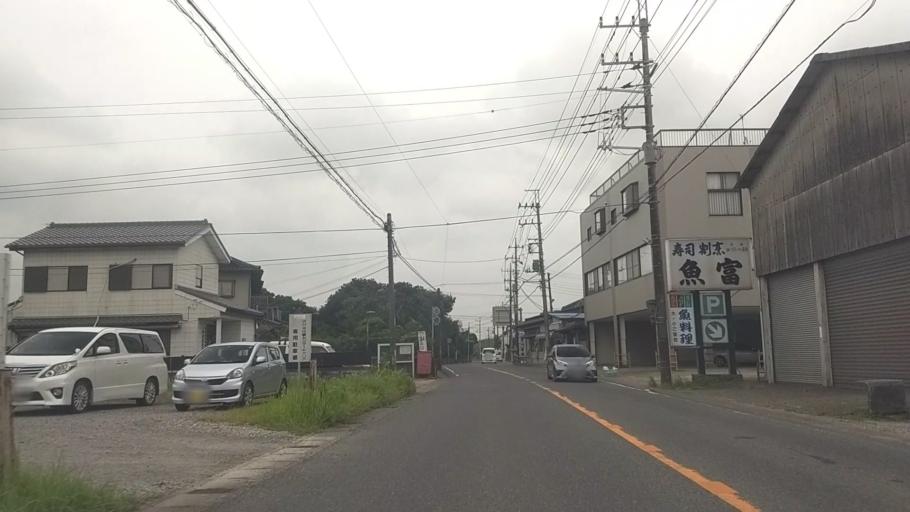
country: JP
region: Chiba
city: Kisarazu
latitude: 35.3841
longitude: 140.0250
